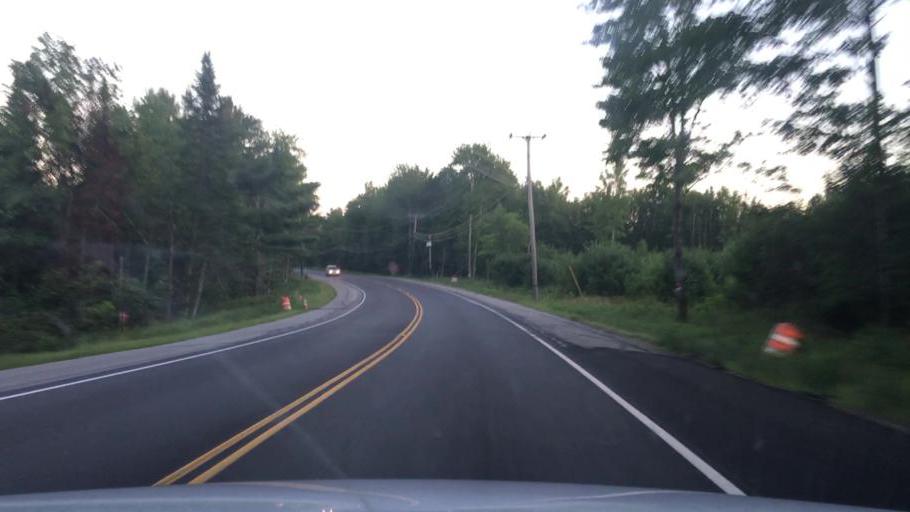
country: US
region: Maine
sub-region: Androscoggin County
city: Turner
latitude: 44.2306
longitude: -70.2542
